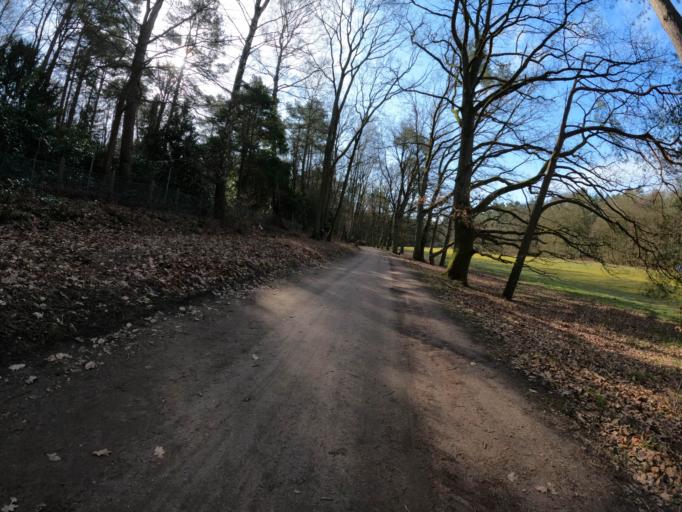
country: DE
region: Lower Saxony
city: Neu Wulmstorf
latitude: 53.4475
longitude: 9.8691
